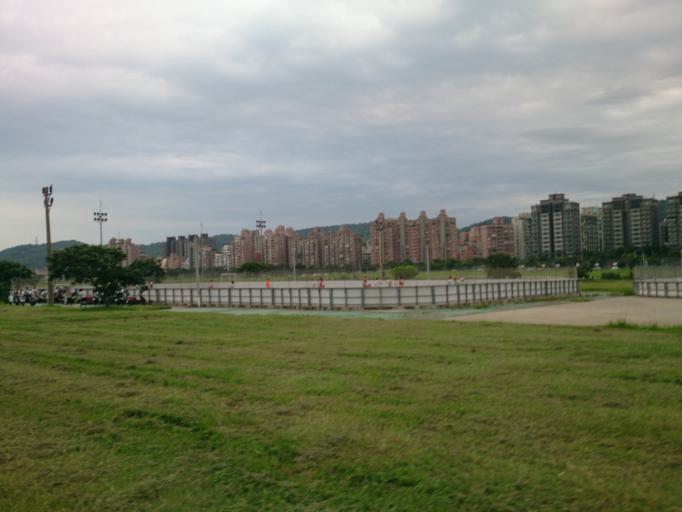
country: TW
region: Taipei
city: Taipei
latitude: 25.0737
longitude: 121.5540
